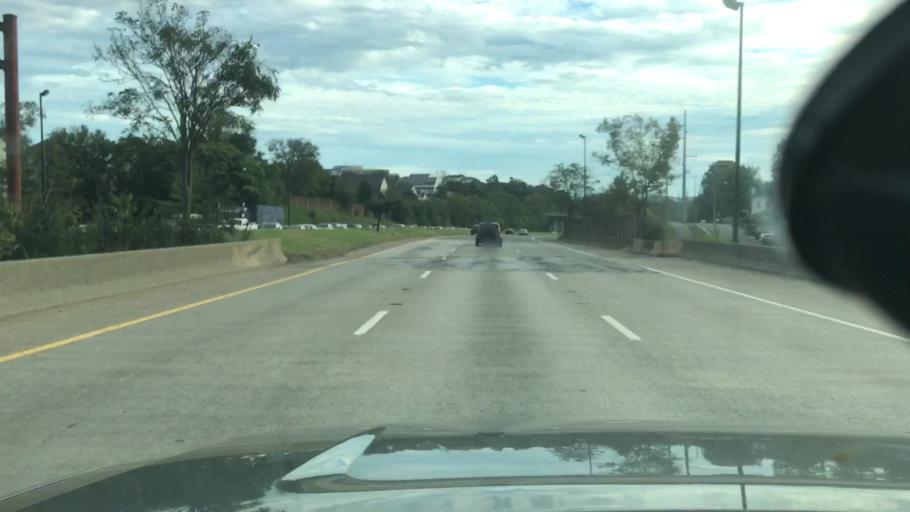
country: US
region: Tennessee
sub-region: Davidson County
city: Nashville
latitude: 36.1476
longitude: -86.8225
